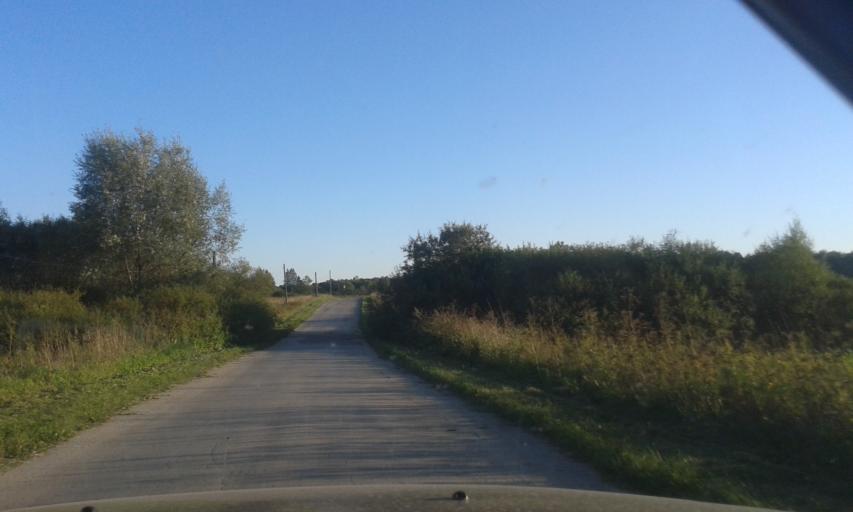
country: RU
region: Tula
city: Krapivna
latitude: 54.1192
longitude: 37.1526
